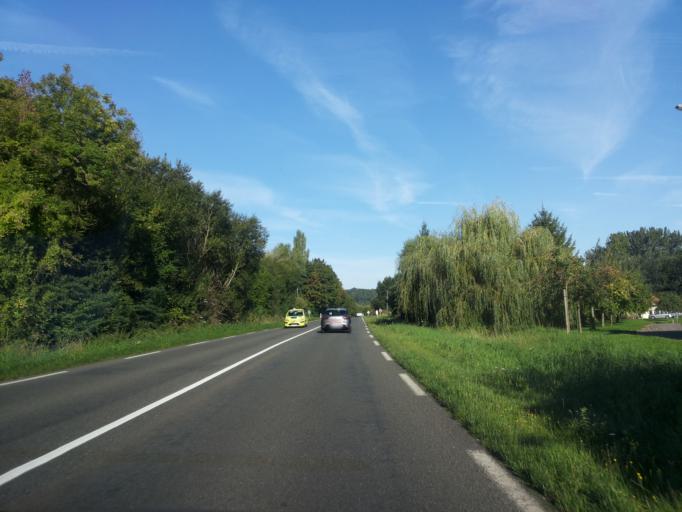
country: FR
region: Picardie
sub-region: Departement de l'Aisne
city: Crepy
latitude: 49.5994
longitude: 3.5158
